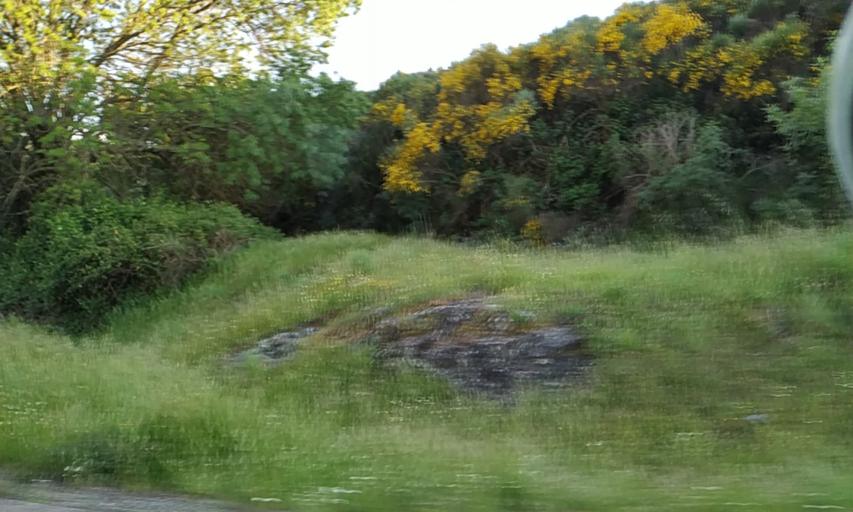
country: PT
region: Portalegre
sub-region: Portalegre
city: Sao Juliao
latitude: 39.3569
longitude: -7.3152
